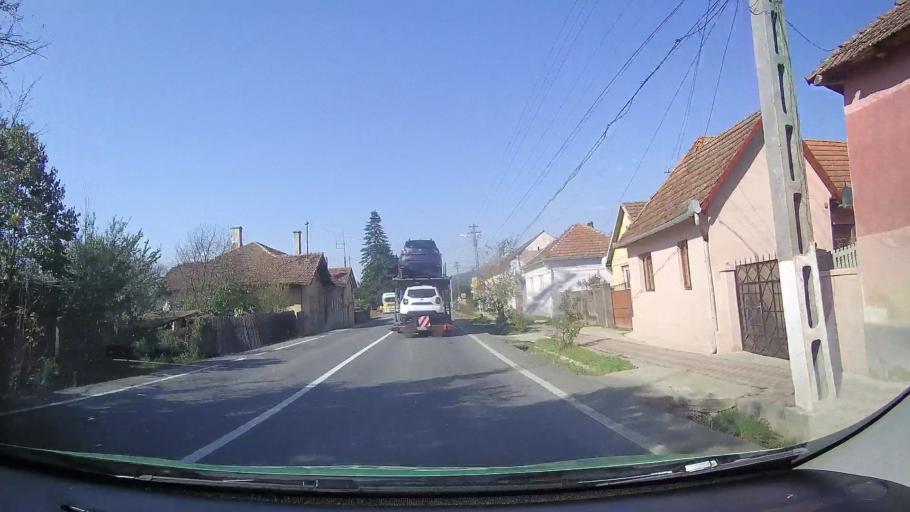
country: RO
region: Arad
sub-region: Comuna Conop
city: Conop
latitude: 46.1009
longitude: 21.8758
